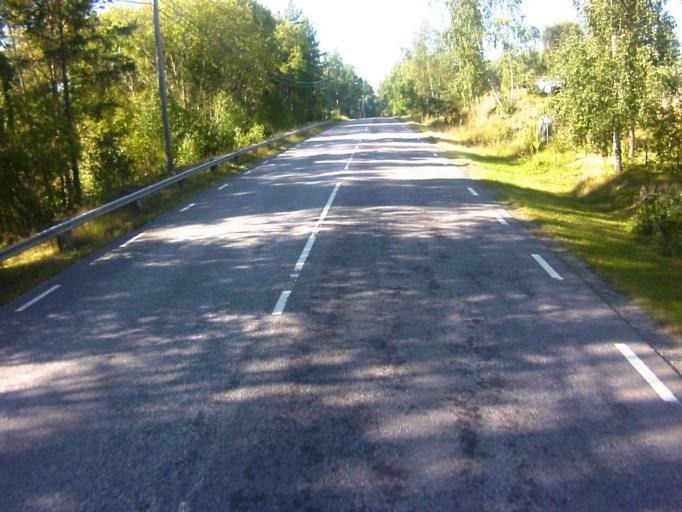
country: SE
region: Soedermanland
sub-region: Eskilstuna Kommun
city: Skogstorp
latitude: 59.3314
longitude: 16.4262
